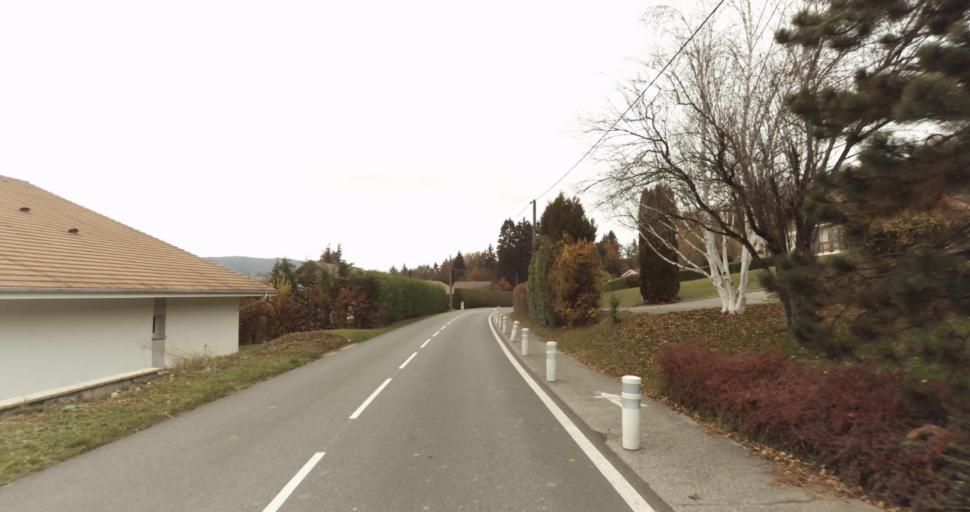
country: FR
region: Rhone-Alpes
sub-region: Departement de la Haute-Savoie
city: Saint-Martin-Bellevue
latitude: 45.9742
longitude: 6.1342
